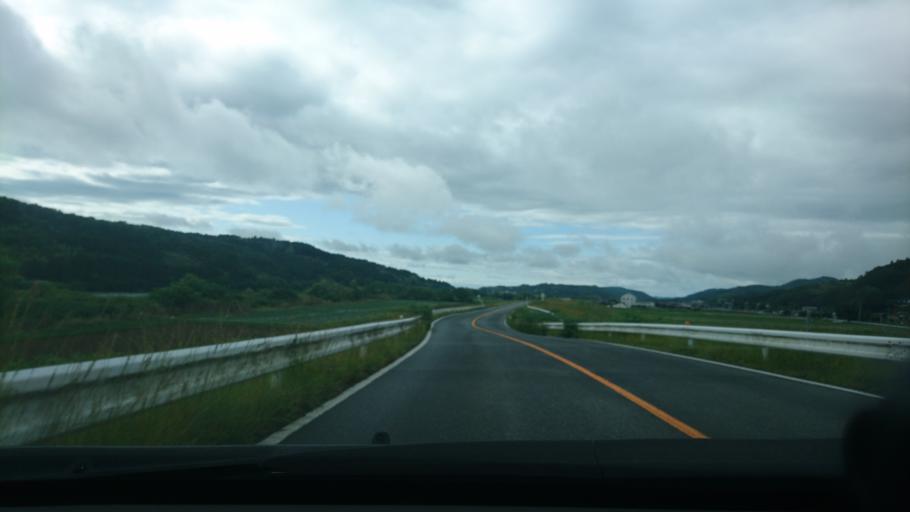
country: JP
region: Miyagi
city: Wakuya
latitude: 38.6346
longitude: 141.2896
